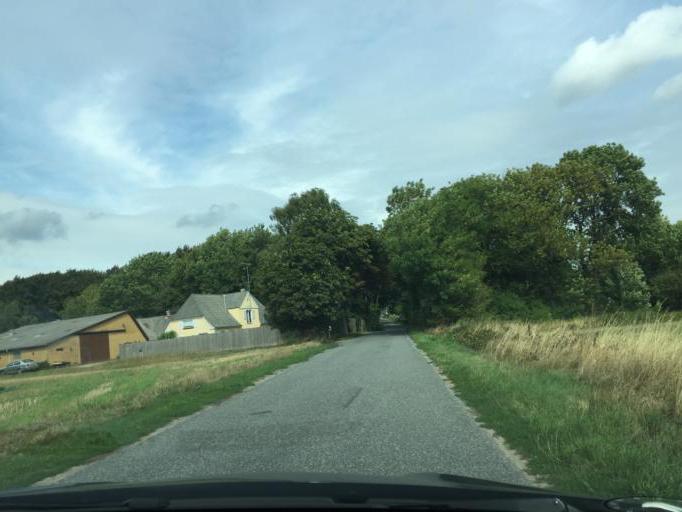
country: DK
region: South Denmark
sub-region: Assens Kommune
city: Vissenbjerg
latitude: 55.3603
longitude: 10.1430
